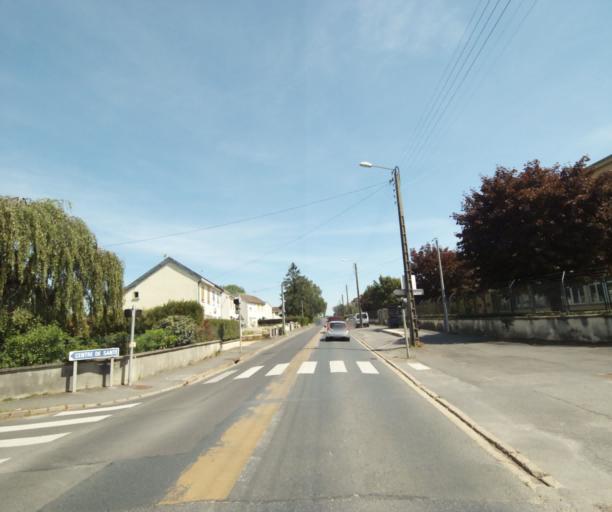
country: FR
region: Champagne-Ardenne
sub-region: Departement des Ardennes
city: Warcq
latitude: 49.7671
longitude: 4.6861
